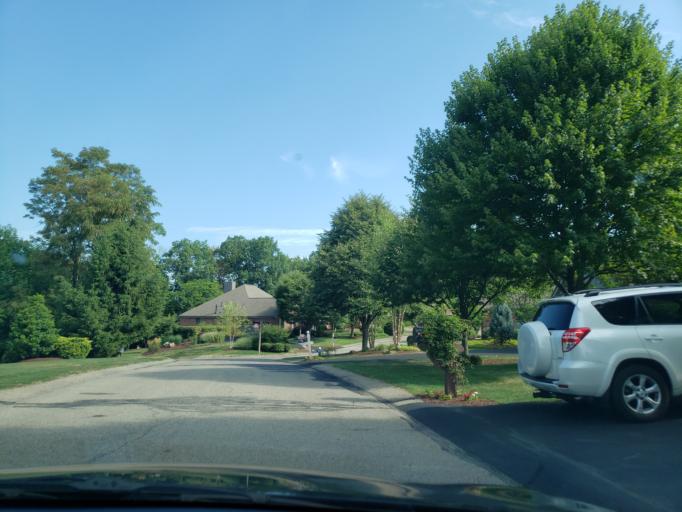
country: US
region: Pennsylvania
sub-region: Allegheny County
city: Coraopolis
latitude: 40.5385
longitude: -80.1470
